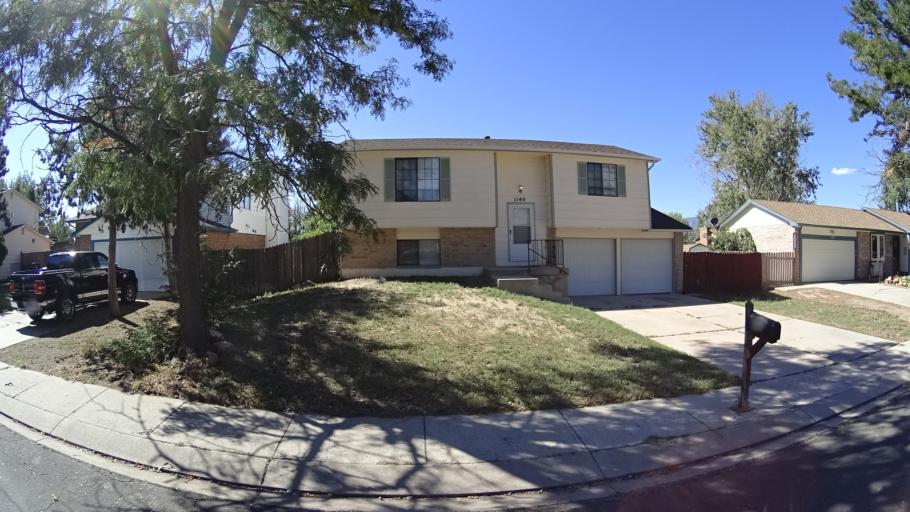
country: US
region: Colorado
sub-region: El Paso County
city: Cimarron Hills
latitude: 38.8153
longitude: -104.7344
